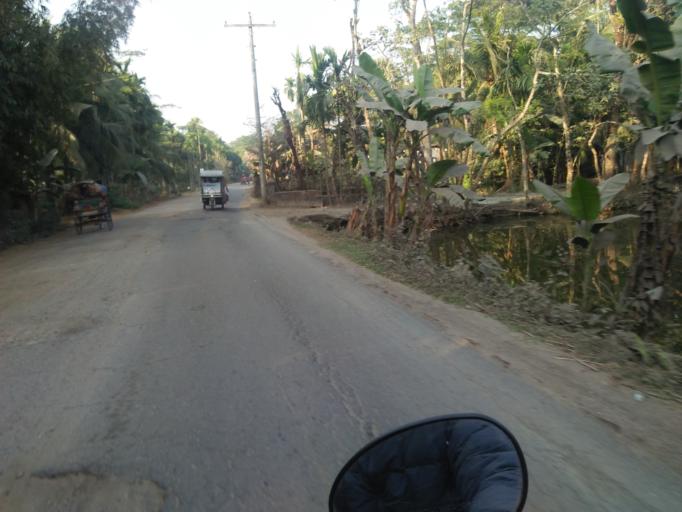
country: BD
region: Barisal
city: Bhola
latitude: 22.7461
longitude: 90.6345
